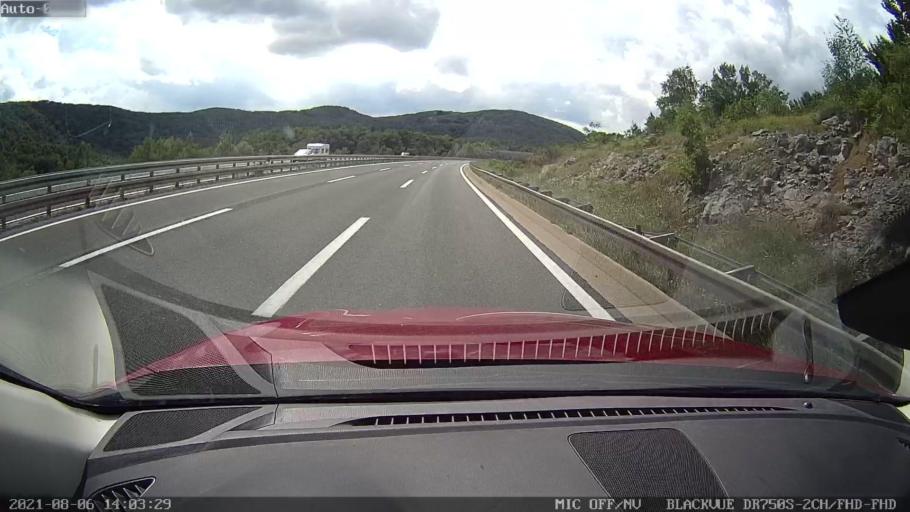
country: HR
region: Primorsko-Goranska
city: Vrbovsko
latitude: 45.3877
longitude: 15.1939
